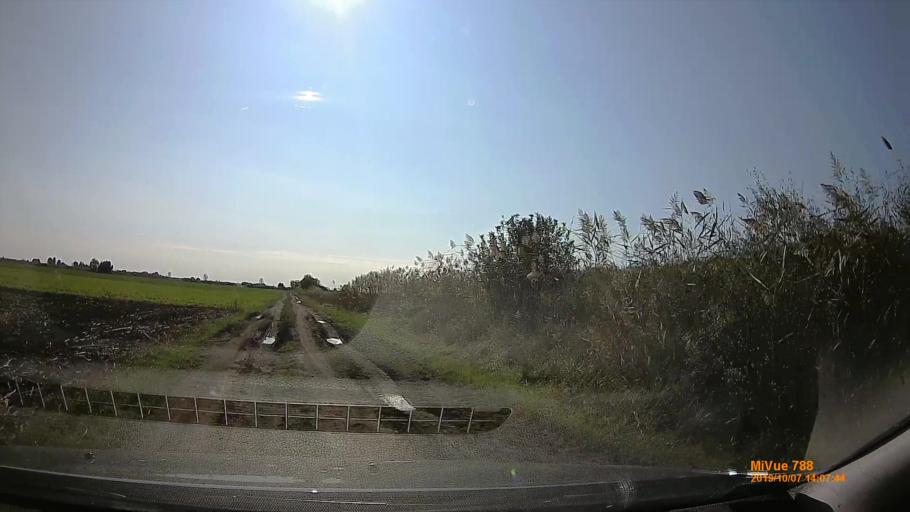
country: HU
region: Jasz-Nagykun-Szolnok
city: Cserkeszolo
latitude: 46.8729
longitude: 20.2265
